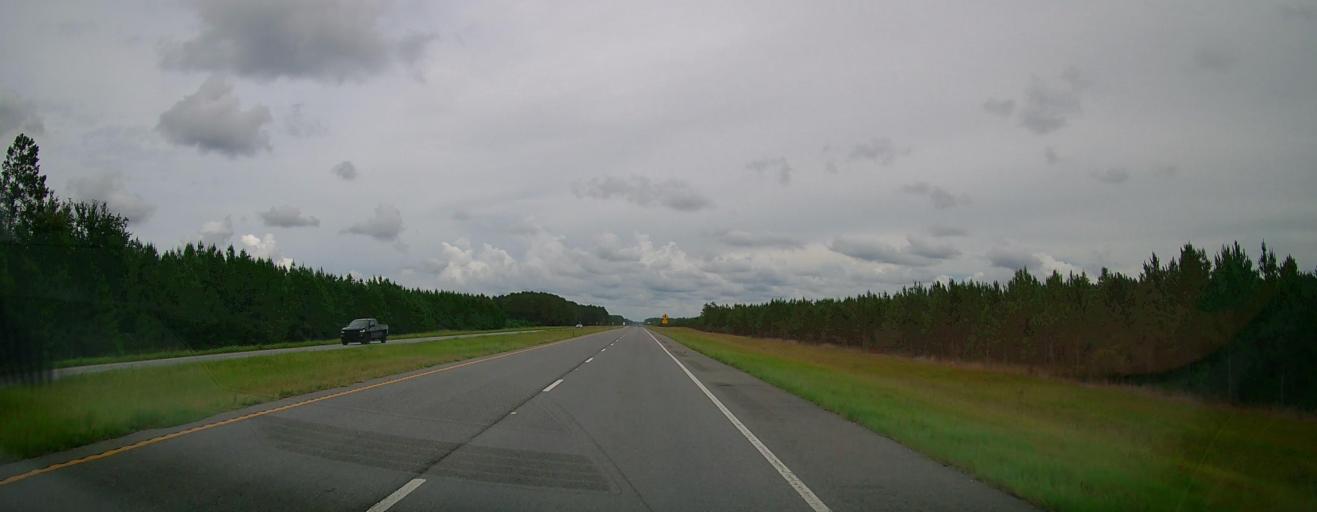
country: US
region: Georgia
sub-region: Appling County
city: Baxley
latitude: 31.7518
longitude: -82.2718
